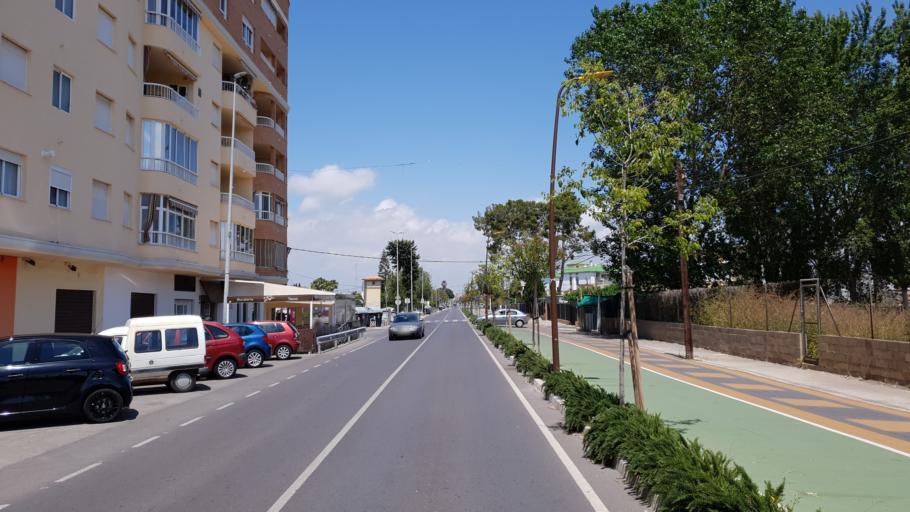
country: ES
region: Valencia
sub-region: Provincia de Castello
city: Burriana
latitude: 39.8668
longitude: -0.0722
